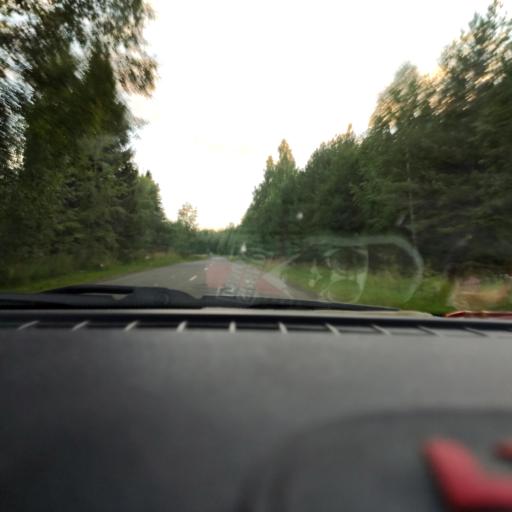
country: RU
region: Perm
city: Ocher
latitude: 57.9366
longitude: 54.7985
